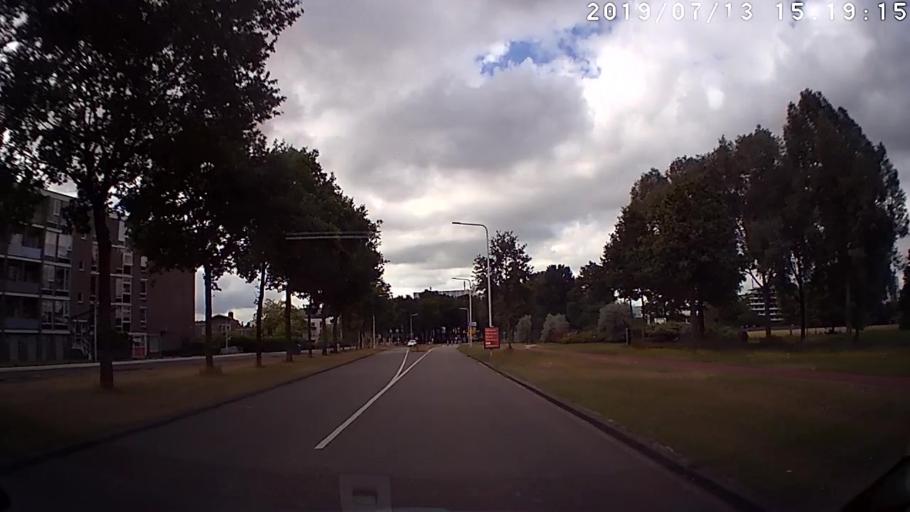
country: NL
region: Overijssel
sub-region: Gemeente Zwolle
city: Zwolle
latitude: 52.5067
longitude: 6.1073
